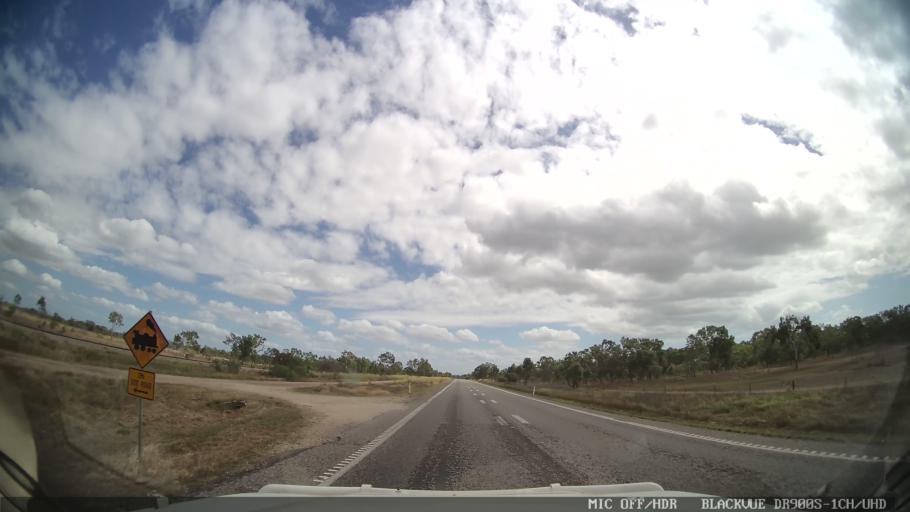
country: AU
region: Queensland
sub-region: Burdekin
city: Home Hill
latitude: -19.9052
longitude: 147.7689
